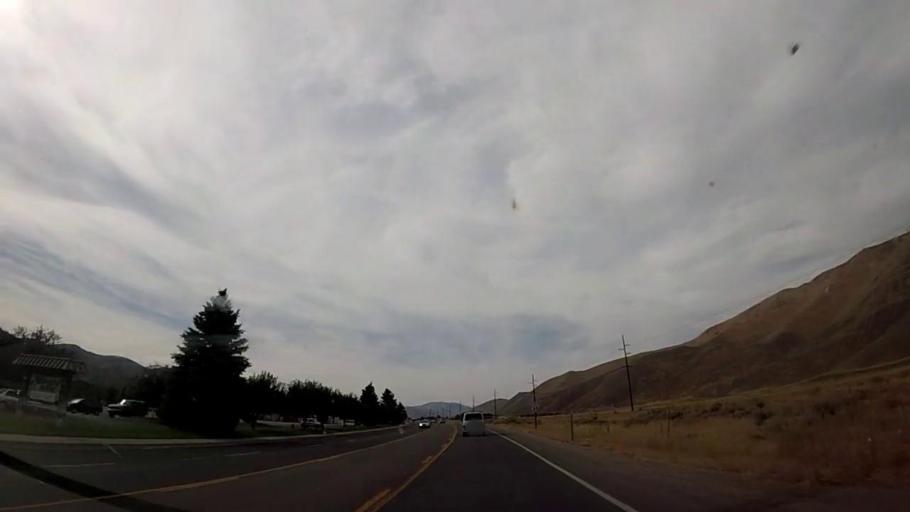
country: US
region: Idaho
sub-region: Blaine County
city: Bellevue
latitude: 43.4742
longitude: -114.2649
